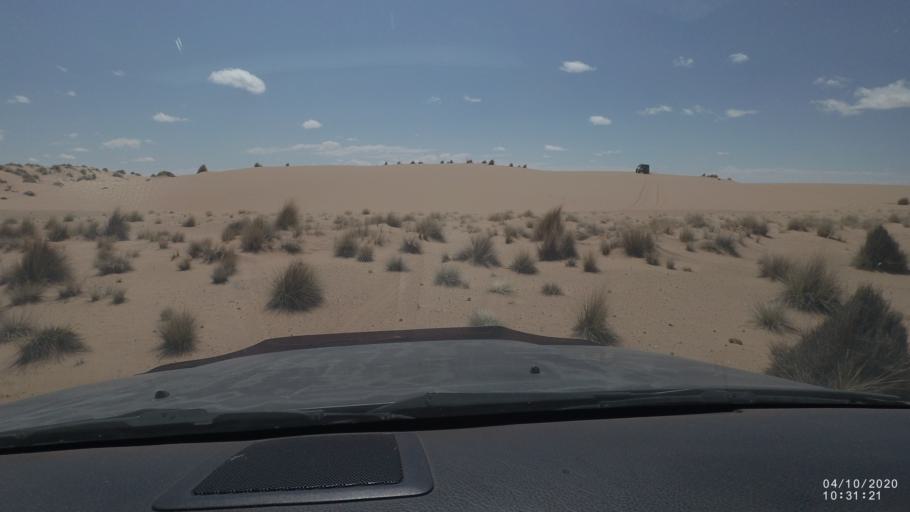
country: BO
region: Oruro
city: Poopo
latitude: -18.7038
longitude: -67.4842
